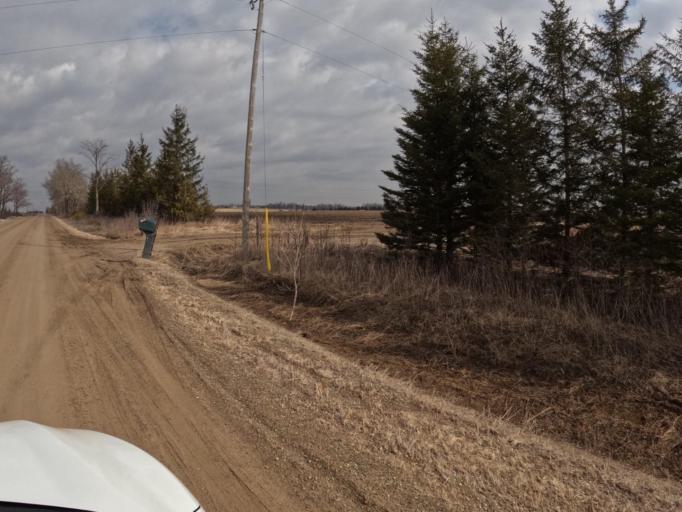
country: CA
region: Ontario
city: Orangeville
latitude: 43.9194
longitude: -80.1853
